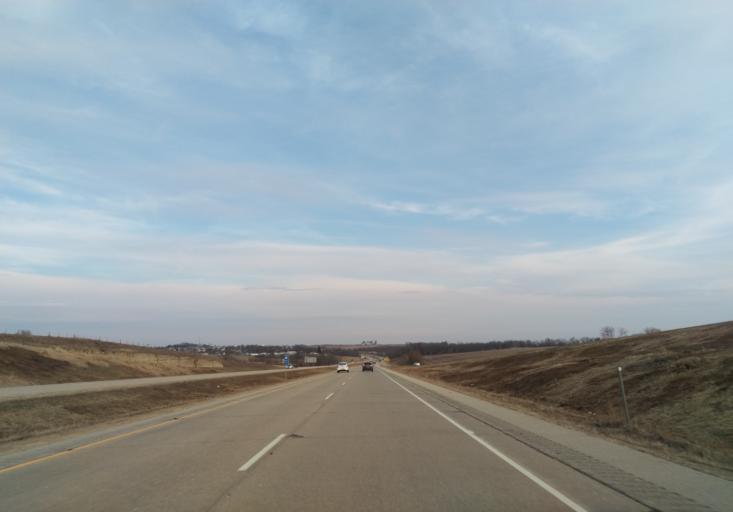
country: US
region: Wisconsin
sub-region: Dane County
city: Mount Horeb
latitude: 43.0003
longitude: -89.7590
